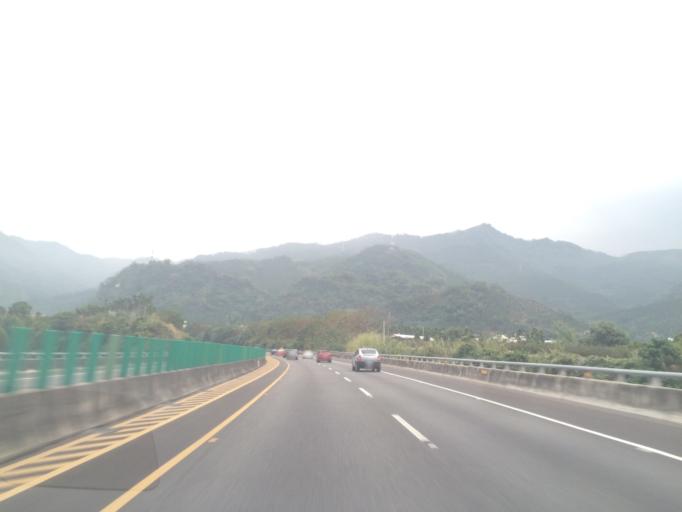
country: TW
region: Taiwan
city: Zhongxing New Village
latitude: 23.9876
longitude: 120.7889
